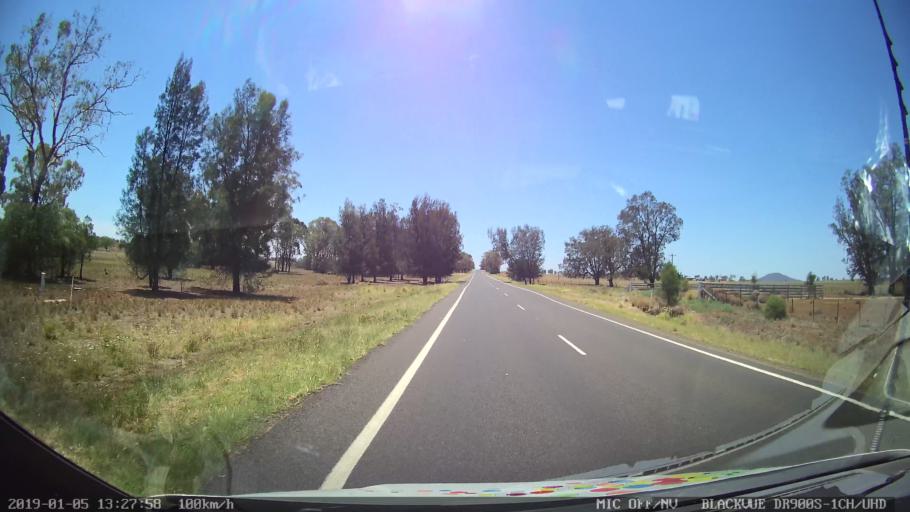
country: AU
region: New South Wales
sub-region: Gunnedah
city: Gunnedah
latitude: -31.0399
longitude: 150.0368
